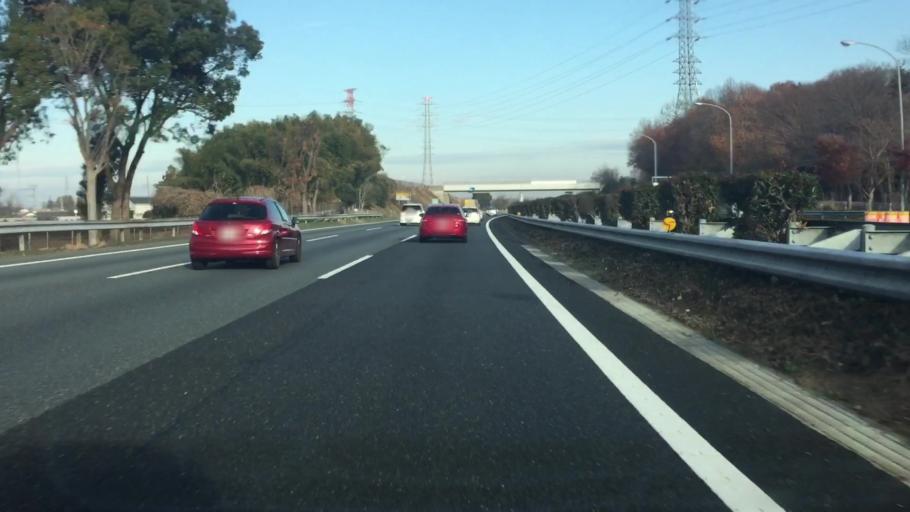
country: JP
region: Saitama
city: Yorii
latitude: 36.1755
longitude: 139.1923
